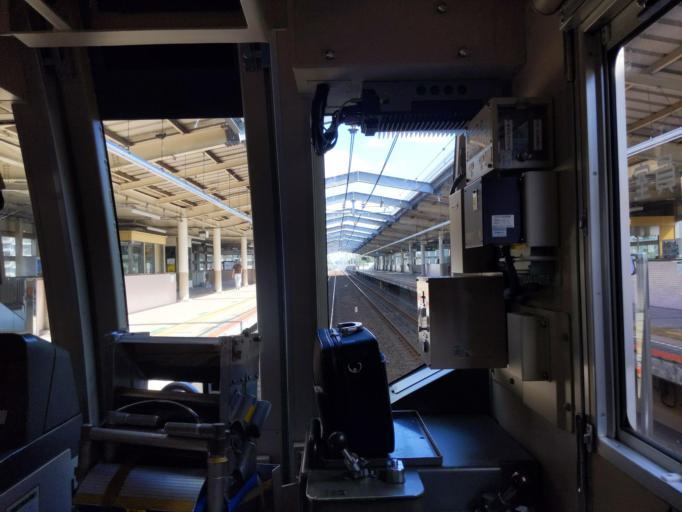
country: JP
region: Chiba
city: Shiroi
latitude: 35.7280
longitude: 140.1032
